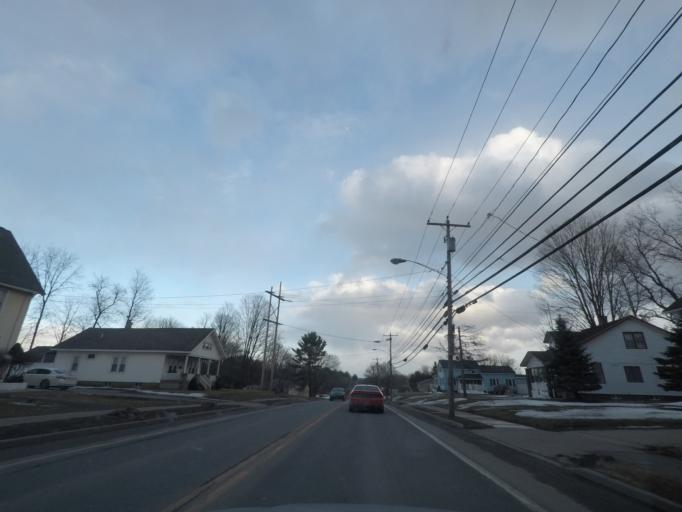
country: US
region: New York
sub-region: Oneida County
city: Utica
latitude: 43.1122
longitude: -75.1926
